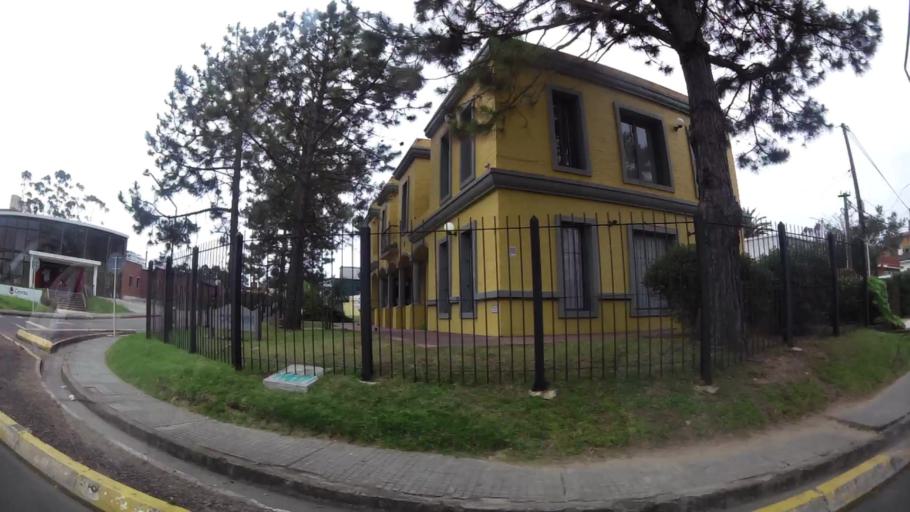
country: UY
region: Maldonado
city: Maldonado
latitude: -34.9127
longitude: -54.9609
